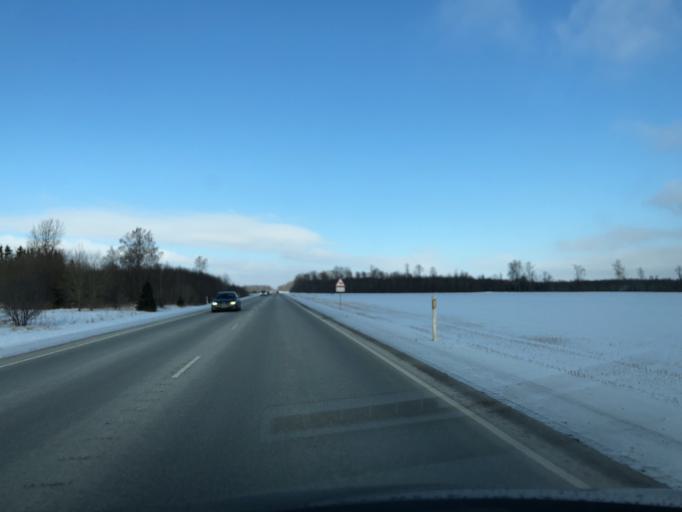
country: EE
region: Jaervamaa
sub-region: Paide linn
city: Paide
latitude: 58.7893
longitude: 25.7582
